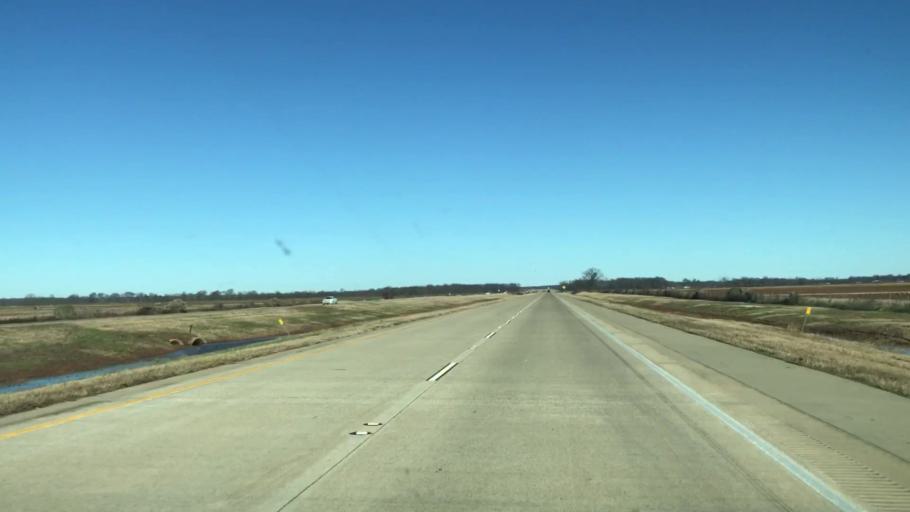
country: US
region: Louisiana
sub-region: Caddo Parish
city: Oil City
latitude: 32.7259
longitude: -93.8712
